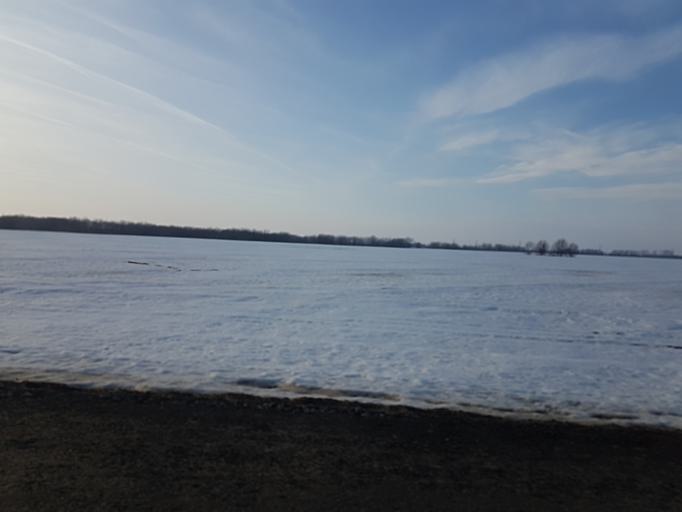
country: RU
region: Tambov
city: Komsomolets
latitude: 52.7347
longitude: 41.2935
